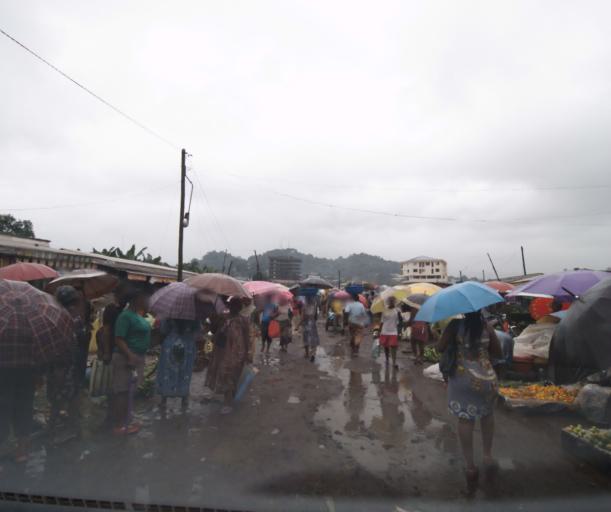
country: CM
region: South-West Province
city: Limbe
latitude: 4.0129
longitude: 9.2099
